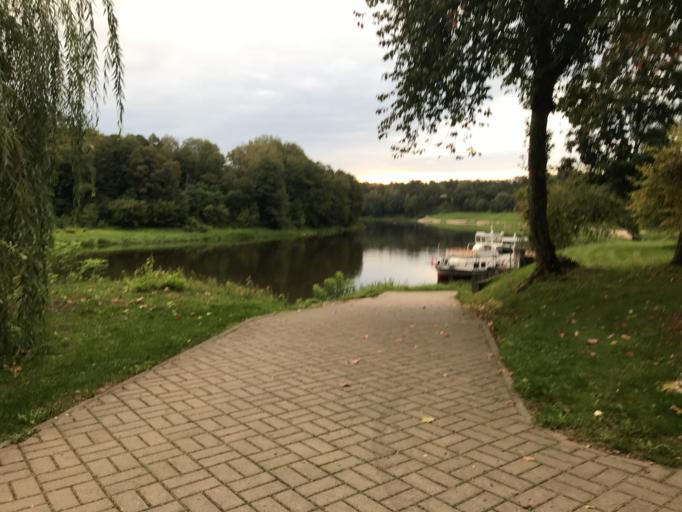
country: LT
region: Alytaus apskritis
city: Druskininkai
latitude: 54.0200
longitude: 23.9789
